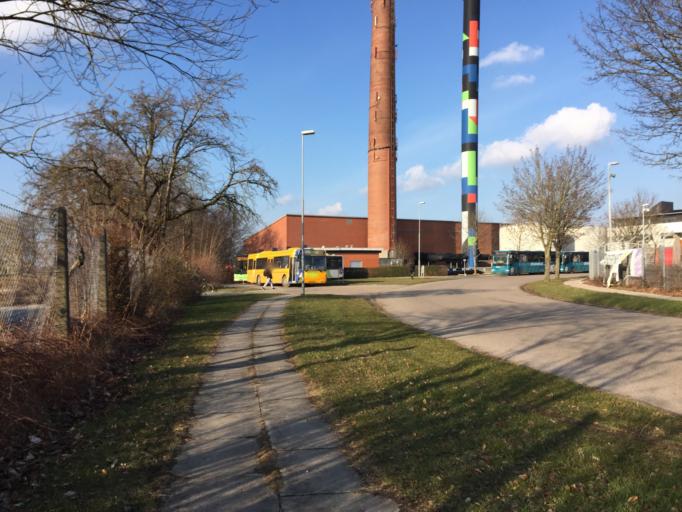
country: DK
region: South Denmark
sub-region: Odense Kommune
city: Odense
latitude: 55.3809
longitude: 10.4142
